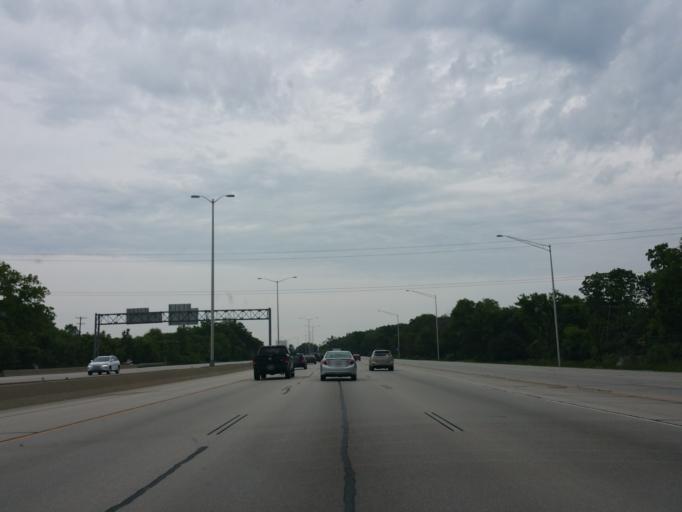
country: US
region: Wisconsin
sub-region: Waukesha County
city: Elm Grove
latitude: 43.0243
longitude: -88.1035
